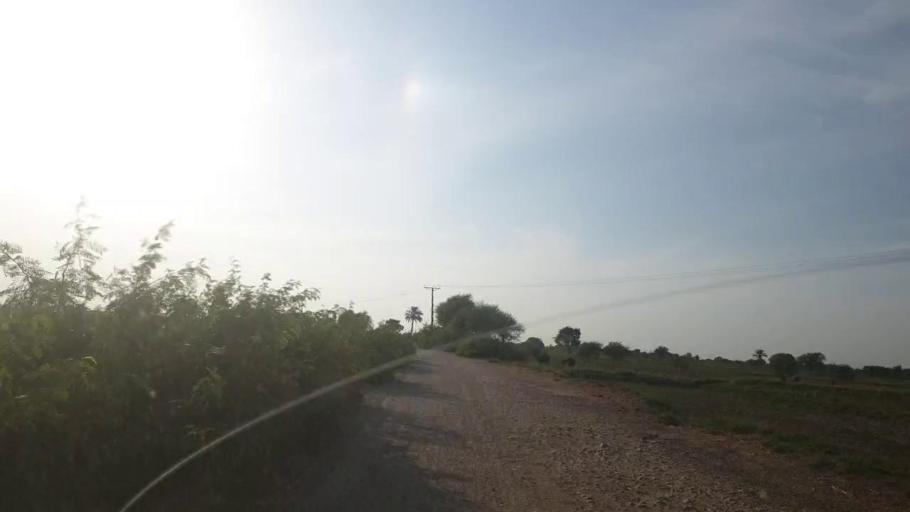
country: PK
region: Sindh
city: Tando Muhammad Khan
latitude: 25.2221
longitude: 68.5364
